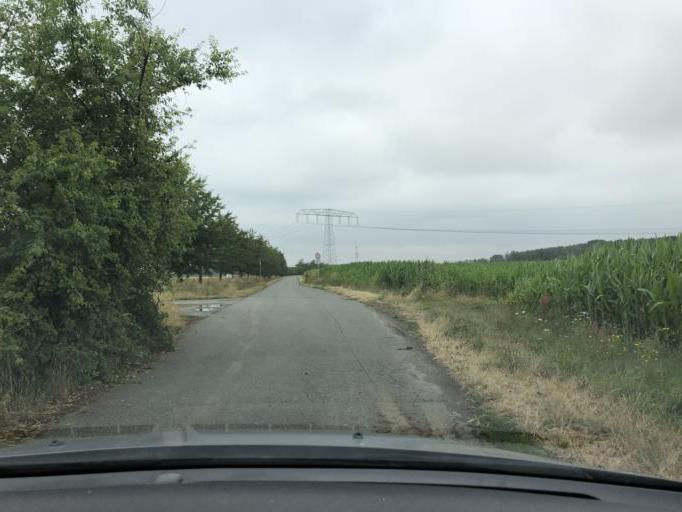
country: DE
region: Saxony
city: Frohburg
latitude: 51.1028
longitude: 12.5613
